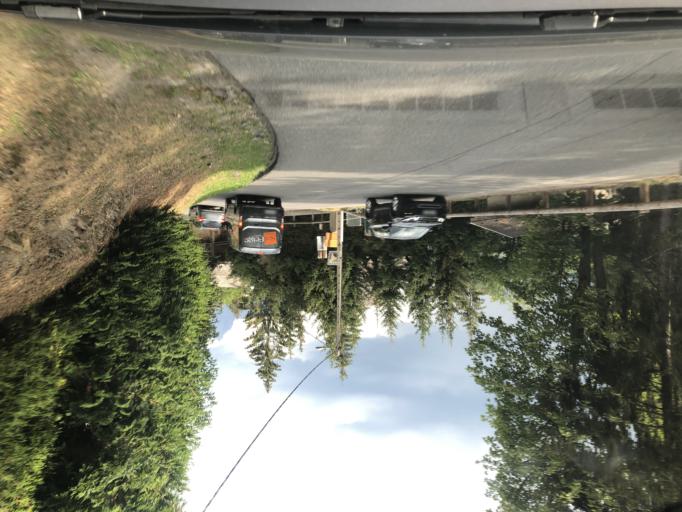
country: FR
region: Rhone-Alpes
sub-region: Departement de la Haute-Savoie
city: Megeve
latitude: 45.8623
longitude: 6.6311
